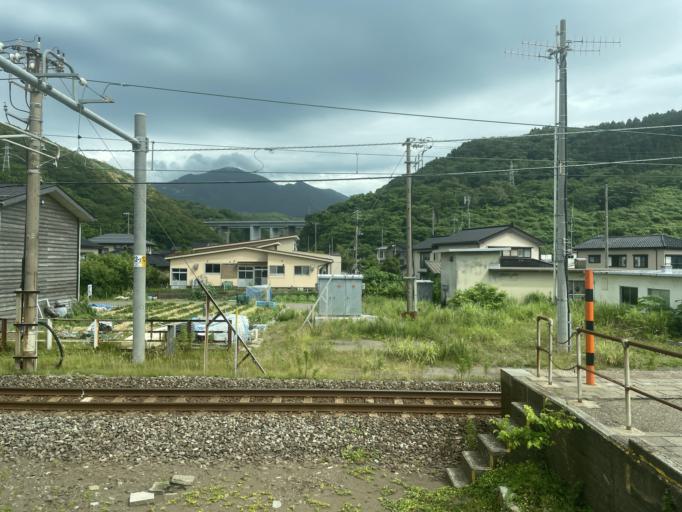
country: JP
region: Niigata
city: Kashiwazaki
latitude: 37.3173
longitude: 138.4319
